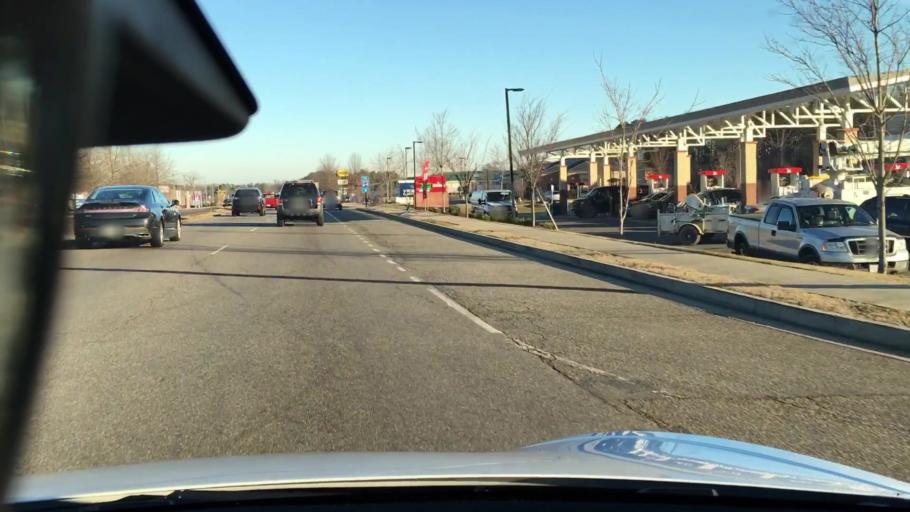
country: US
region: Virginia
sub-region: Henrico County
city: Fort Lee
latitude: 37.5117
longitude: -77.3495
